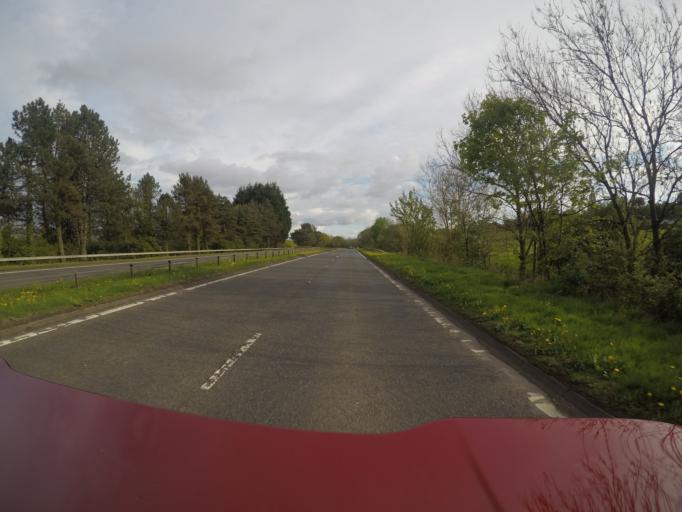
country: GB
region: Scotland
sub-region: West Dunbartonshire
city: Alexandria
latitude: 55.9861
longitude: -4.5880
